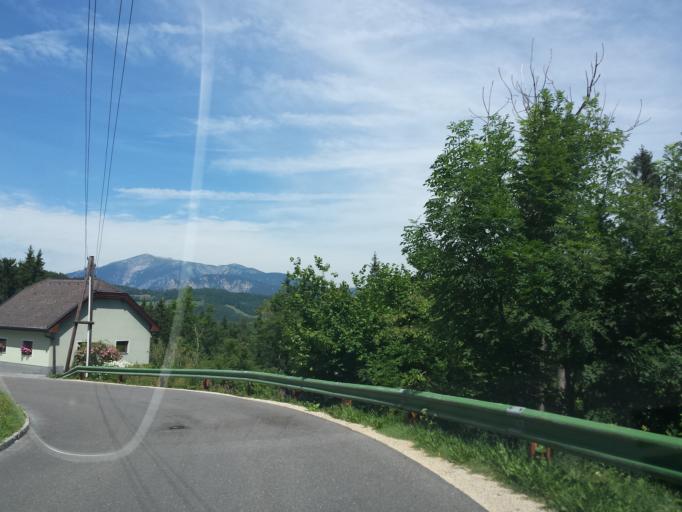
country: AT
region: Lower Austria
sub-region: Politischer Bezirk Neunkirchen
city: Semmering
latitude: 47.6358
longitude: 15.8346
